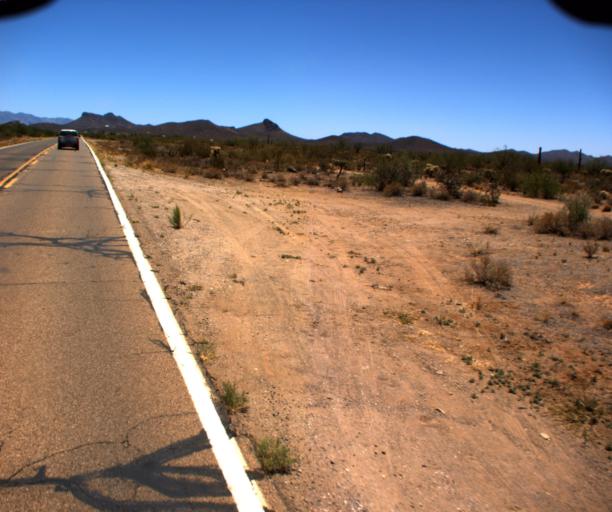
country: US
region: Arizona
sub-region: Pima County
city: Sells
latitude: 31.9300
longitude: -111.9064
